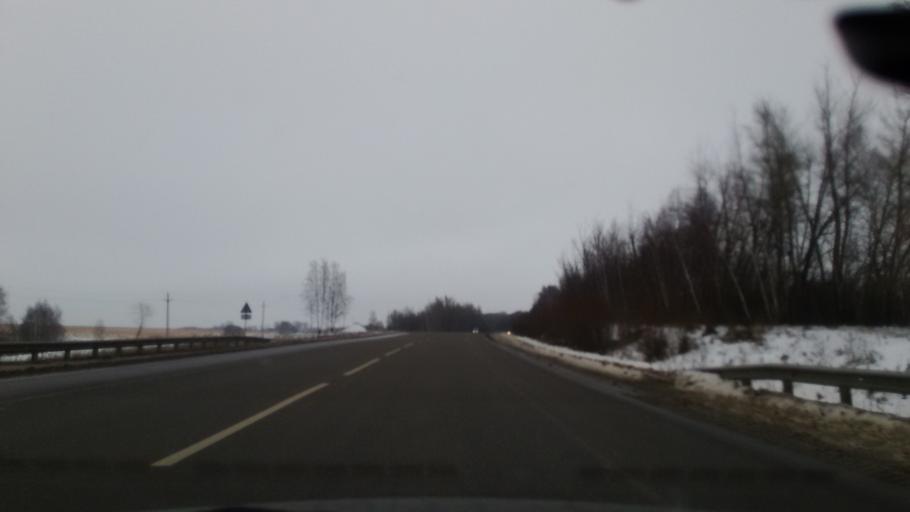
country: RU
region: Tula
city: Bolokhovo
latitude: 54.0370
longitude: 37.8745
